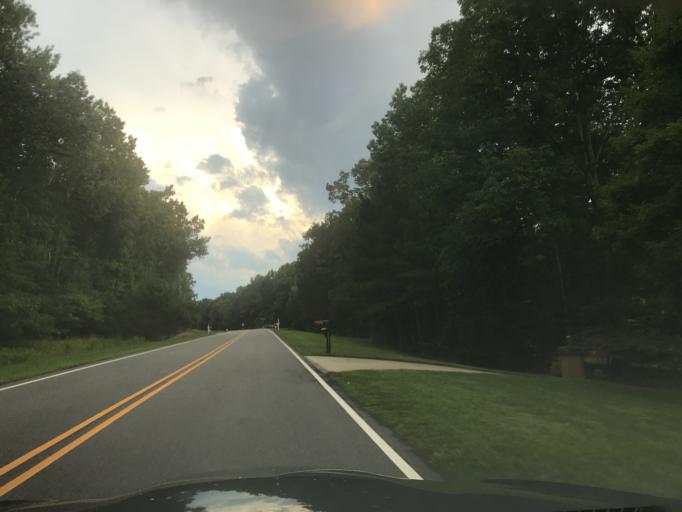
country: US
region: North Carolina
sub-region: Wake County
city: Wake Forest
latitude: 35.9488
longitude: -78.6103
